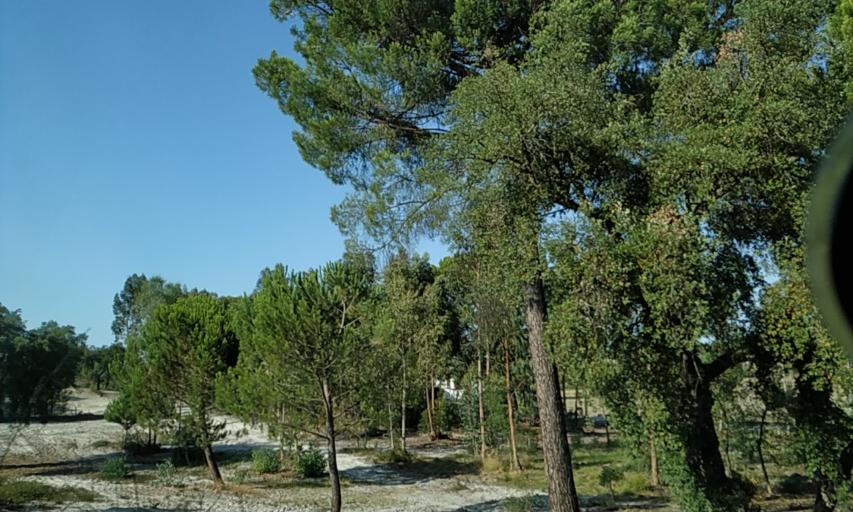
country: PT
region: Santarem
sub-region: Coruche
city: Coruche
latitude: 38.9712
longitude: -8.5378
